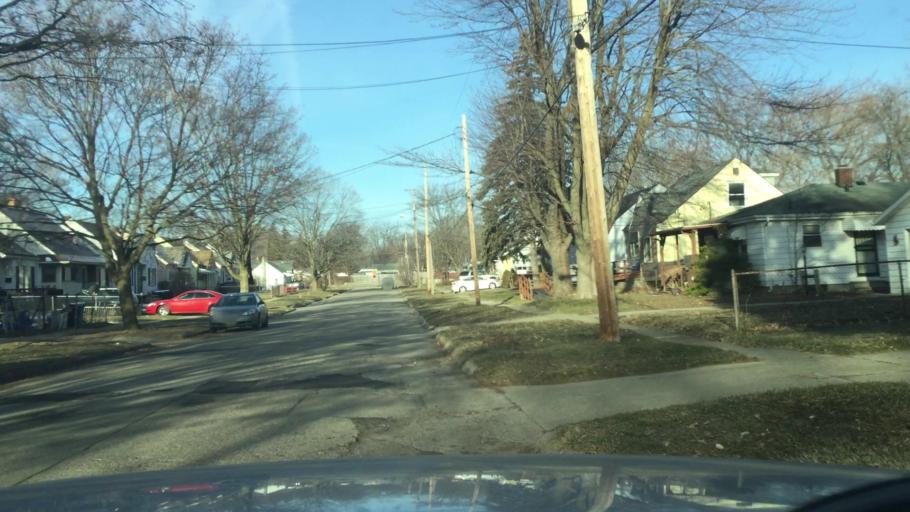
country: US
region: Michigan
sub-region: Genesee County
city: Flint
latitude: 42.9891
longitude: -83.7009
